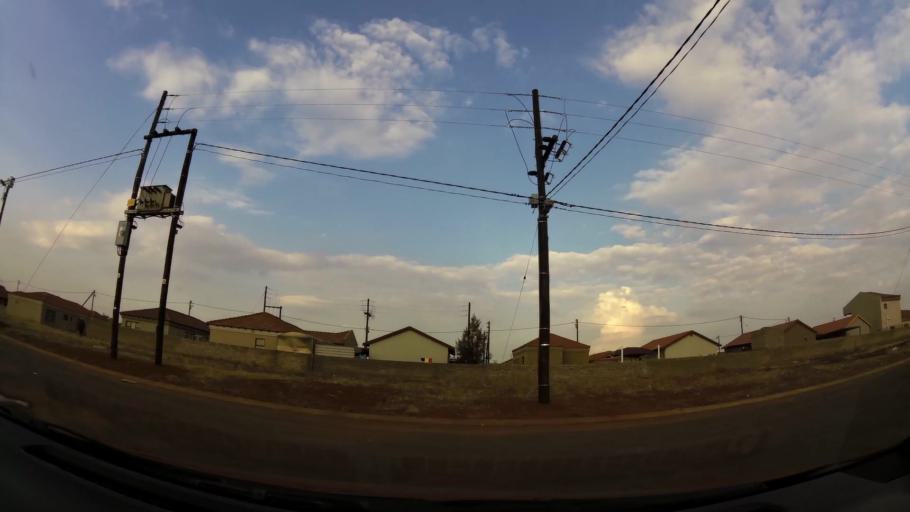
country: ZA
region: Gauteng
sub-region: Sedibeng District Municipality
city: Vanderbijlpark
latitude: -26.6088
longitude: 27.8114
